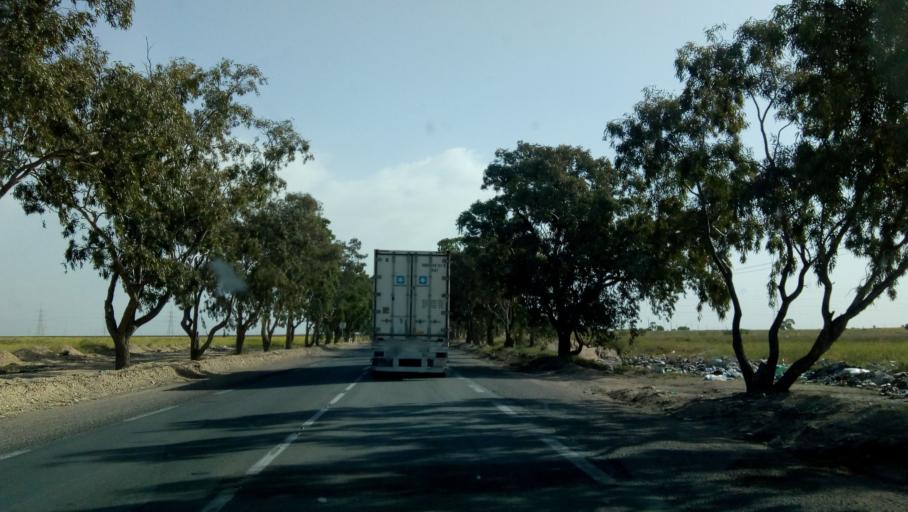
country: TN
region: Qabis
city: Gabes
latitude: 33.8903
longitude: 10.0287
